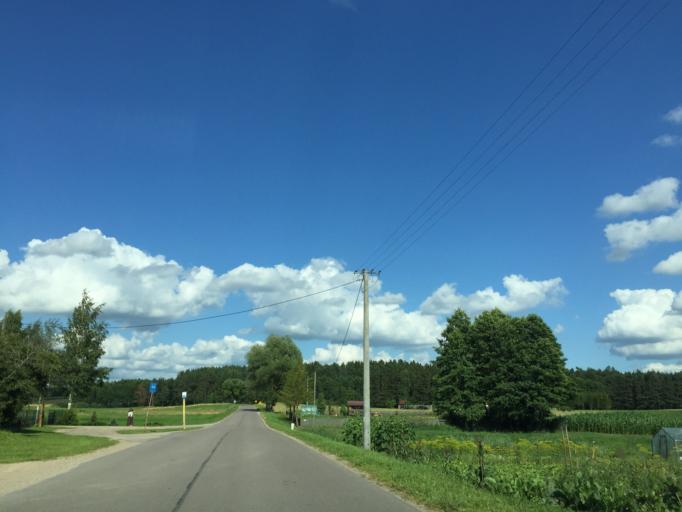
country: PL
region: Podlasie
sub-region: Suwalki
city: Suwalki
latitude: 54.1457
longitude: 23.0585
